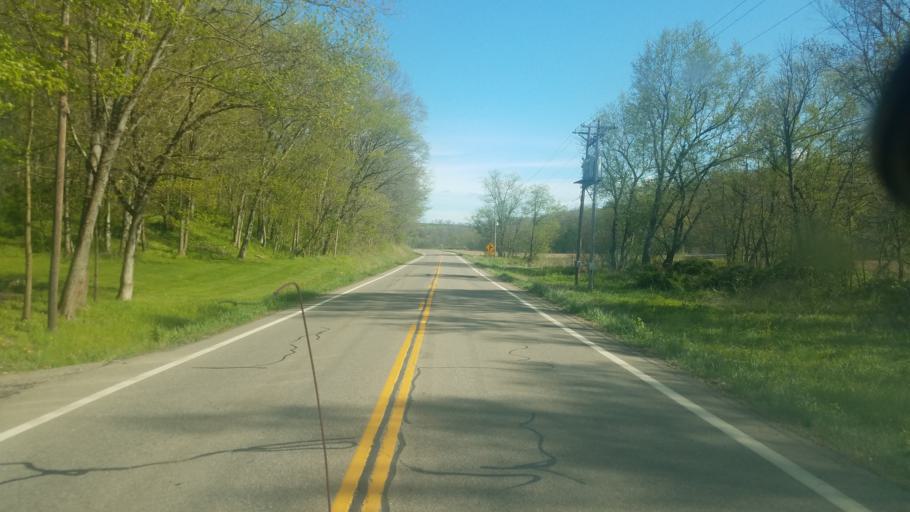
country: US
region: Ohio
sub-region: Coshocton County
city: Coshocton
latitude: 40.3392
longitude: -81.8808
